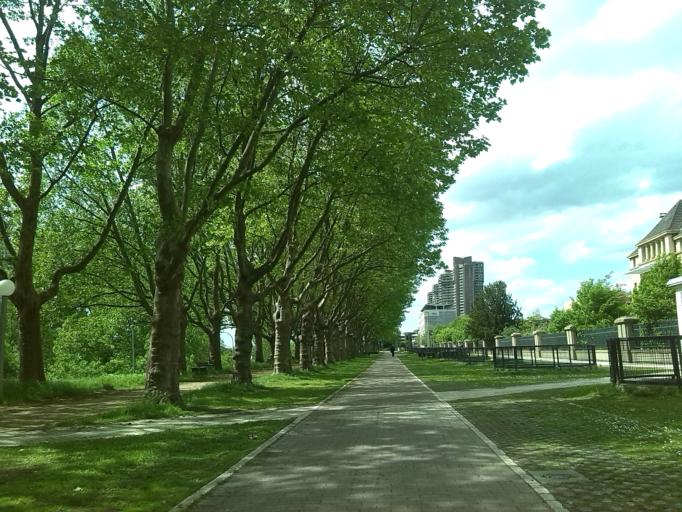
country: DE
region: Baden-Wuerttemberg
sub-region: Karlsruhe Region
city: Mannheim
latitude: 49.4914
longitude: 8.4859
